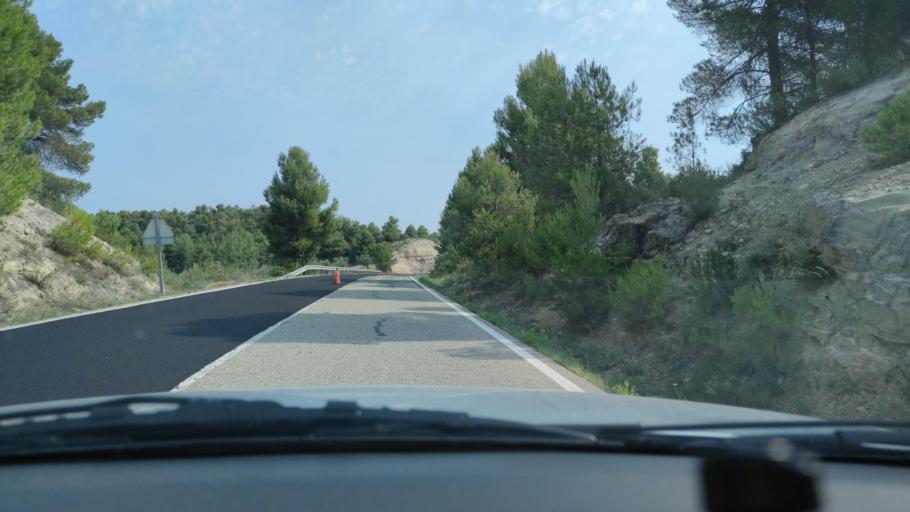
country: ES
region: Catalonia
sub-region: Provincia de Lleida
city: Fulleda
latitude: 41.5093
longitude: 1.0211
